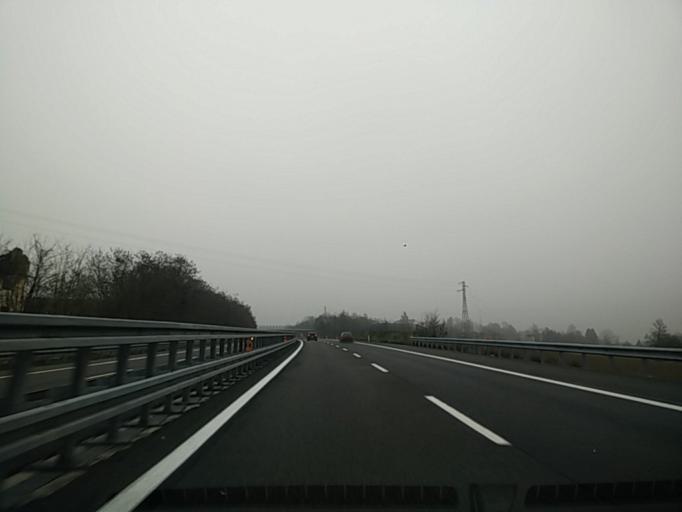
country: IT
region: Piedmont
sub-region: Provincia di Asti
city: Baldichieri d'Asti
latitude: 44.9015
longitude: 8.1233
